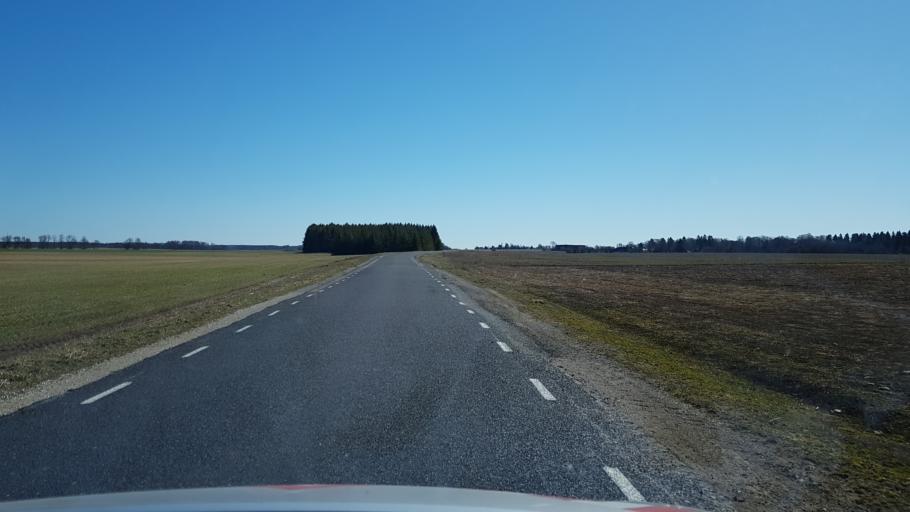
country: EE
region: Laeaene-Virumaa
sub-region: Haljala vald
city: Haljala
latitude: 59.4406
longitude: 26.1564
